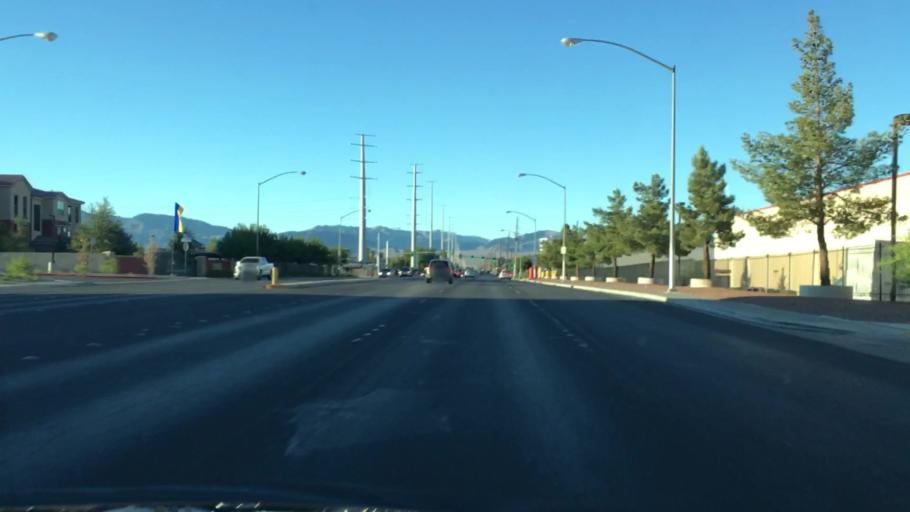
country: US
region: Nevada
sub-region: Clark County
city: Nellis Air Force Base
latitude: 36.2382
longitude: -115.0800
